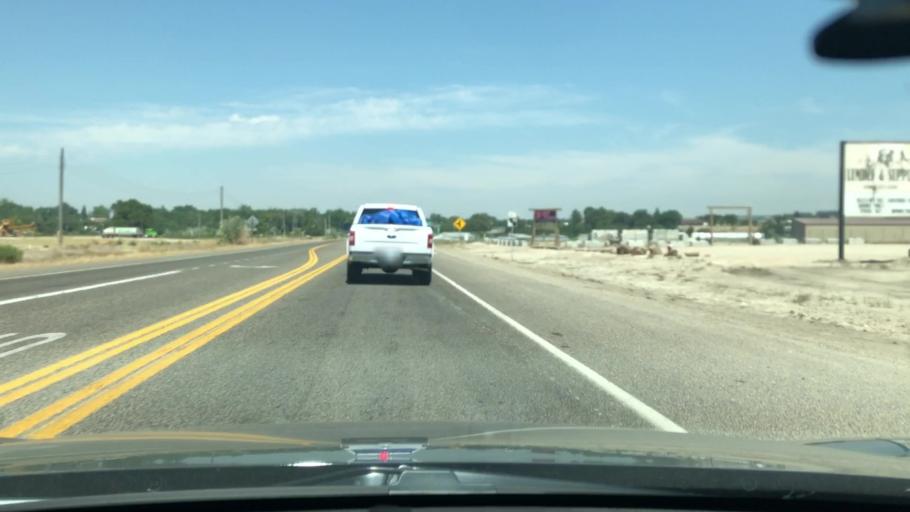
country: US
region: Idaho
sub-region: Owyhee County
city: Homedale
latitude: 43.6144
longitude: -116.9272
